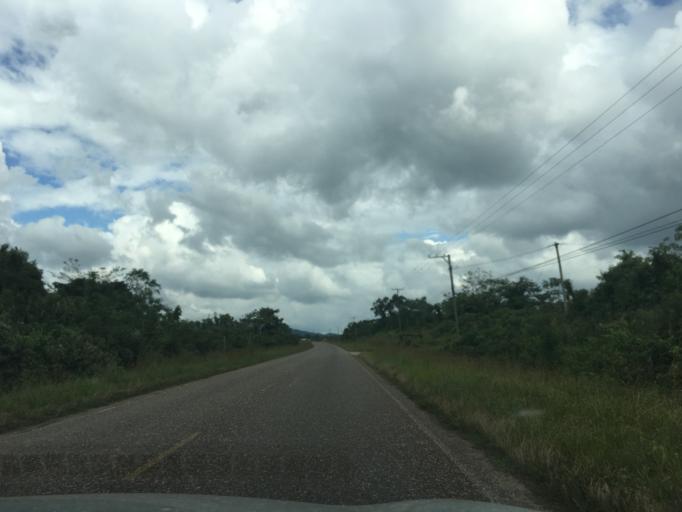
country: BZ
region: Stann Creek
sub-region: Dangriga
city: Dangriga
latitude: 16.9145
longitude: -88.3423
